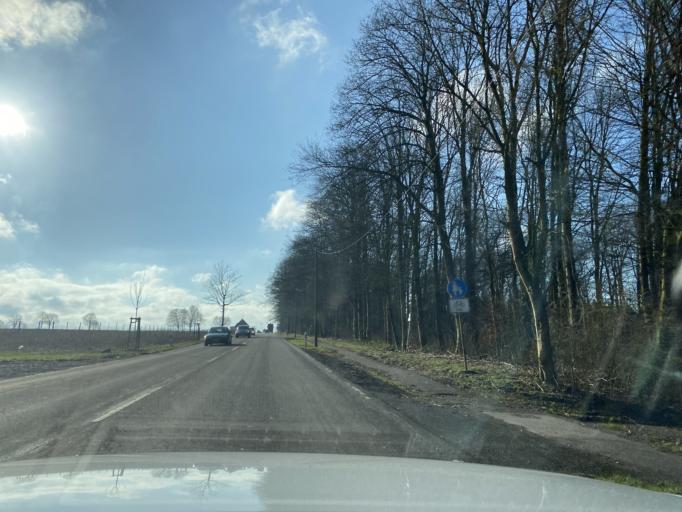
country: DE
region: North Rhine-Westphalia
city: Wermelskirchen
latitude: 51.1699
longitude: 7.2628
